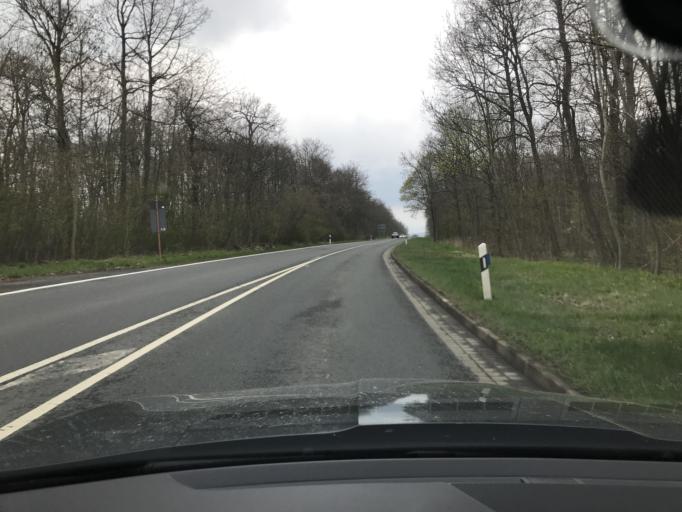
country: DE
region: Saxony-Anhalt
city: Harzgerode
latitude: 51.6231
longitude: 11.1505
